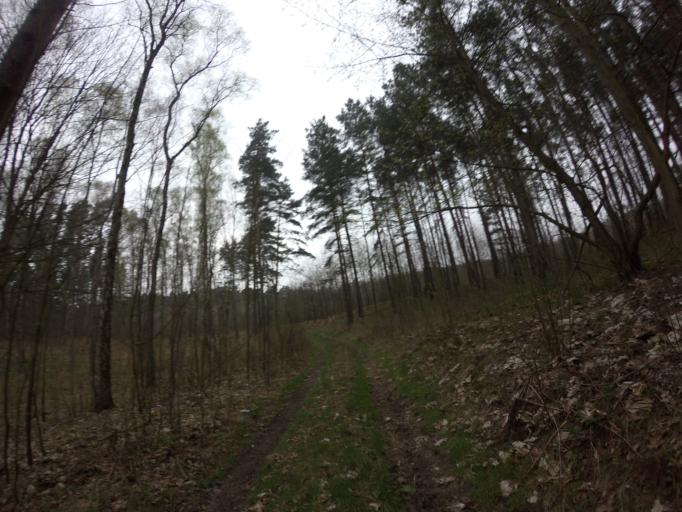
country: PL
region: West Pomeranian Voivodeship
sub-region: Powiat choszczenski
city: Recz
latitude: 53.1845
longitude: 15.5235
